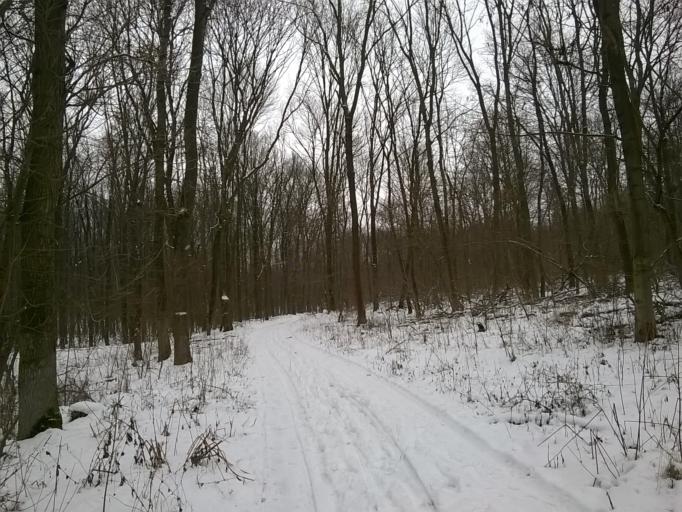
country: SK
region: Nitriansky
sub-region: Okres Nitra
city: Nitra
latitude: 48.2775
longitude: 18.0074
